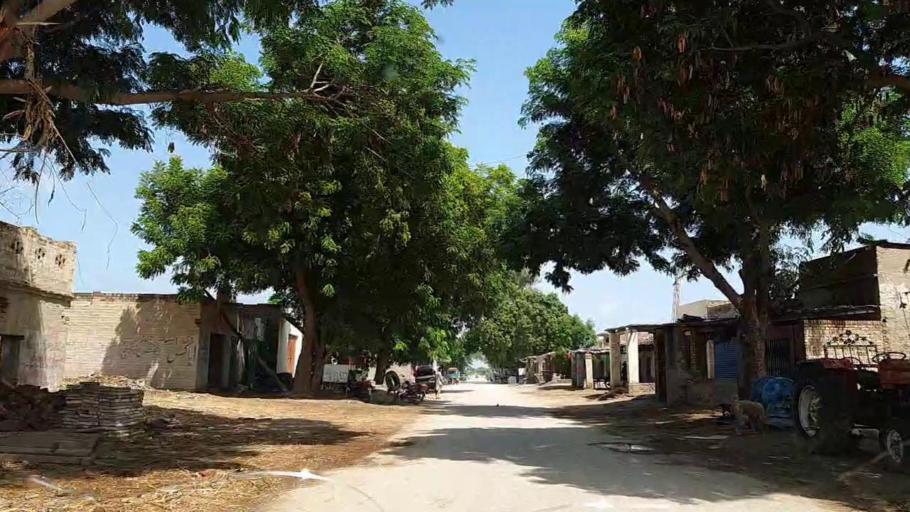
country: PK
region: Sindh
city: Pad Idan
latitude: 26.7979
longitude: 68.2335
